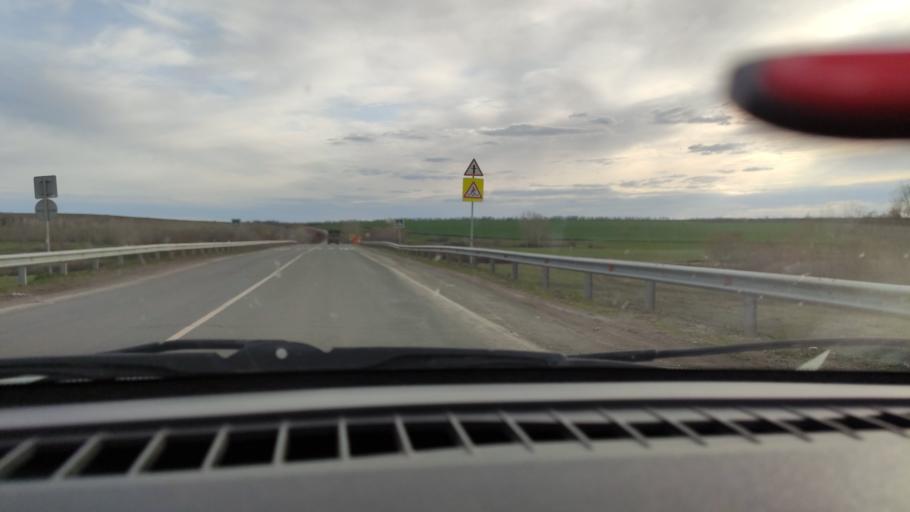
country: RU
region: Orenburg
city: Sakmara
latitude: 52.1933
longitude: 55.3041
